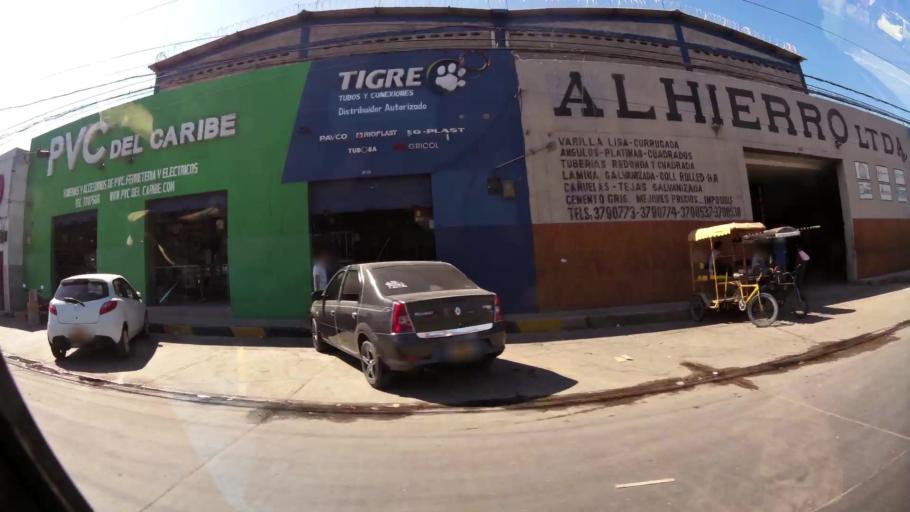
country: CO
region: Atlantico
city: Barranquilla
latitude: 10.9729
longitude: -74.7791
